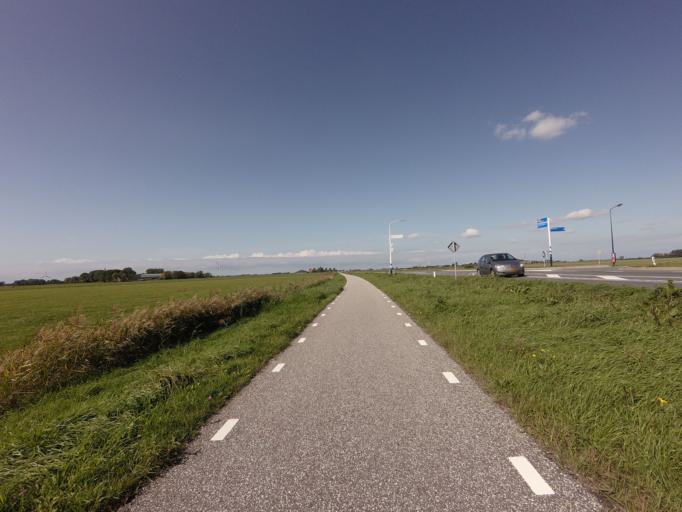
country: NL
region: Friesland
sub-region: Gemeente Littenseradiel
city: Makkum
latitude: 53.1104
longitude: 5.6868
